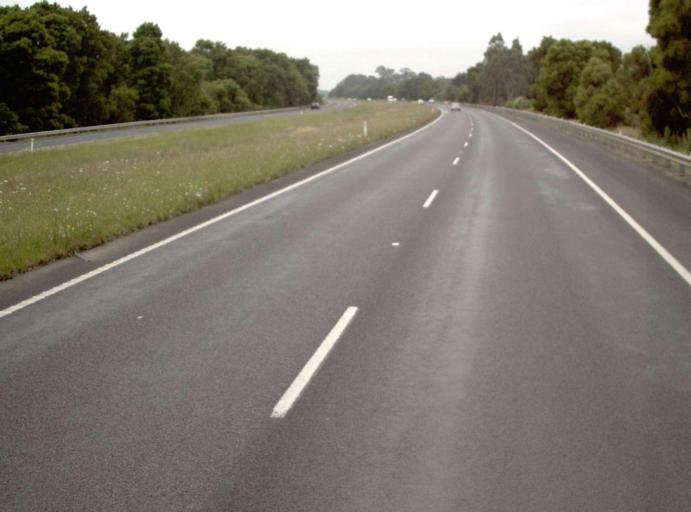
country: AU
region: Victoria
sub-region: Baw Baw
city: Warragul
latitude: -38.1112
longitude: 145.8594
